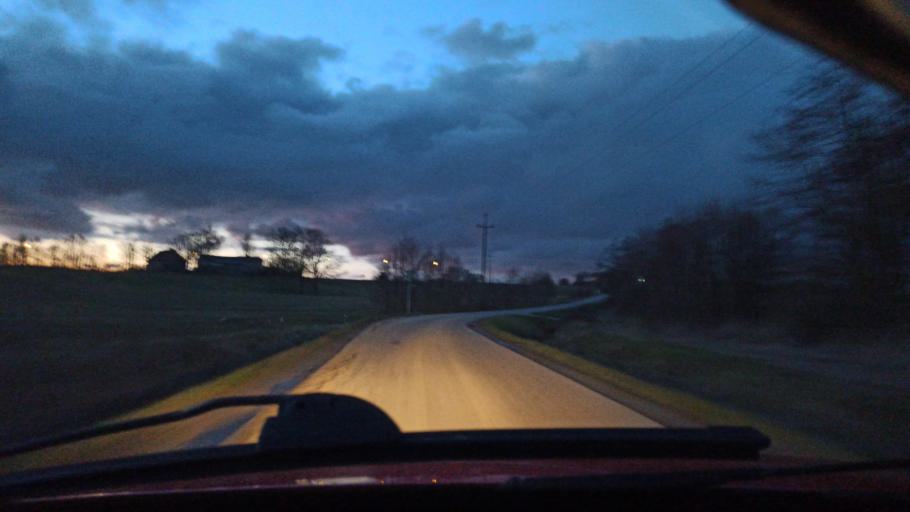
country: PL
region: Warmian-Masurian Voivodeship
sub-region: Powiat elblaski
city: Gronowo Gorne
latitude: 54.1682
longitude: 19.5356
